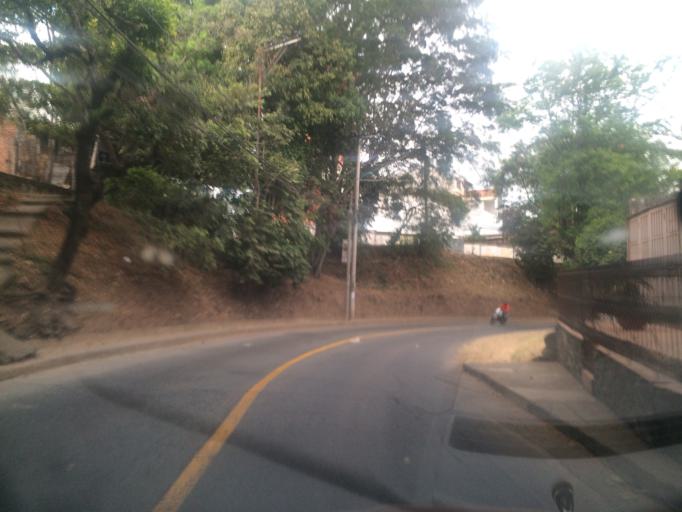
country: CO
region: Valle del Cauca
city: Cali
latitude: 3.4470
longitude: -76.5496
